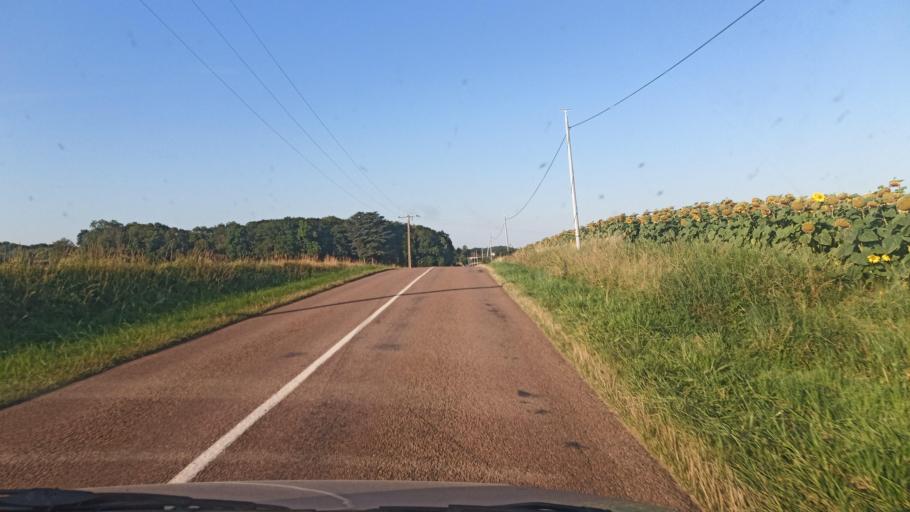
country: FR
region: Bourgogne
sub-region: Departement de l'Yonne
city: Pont-sur-Yonne
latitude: 48.2525
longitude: 3.1660
